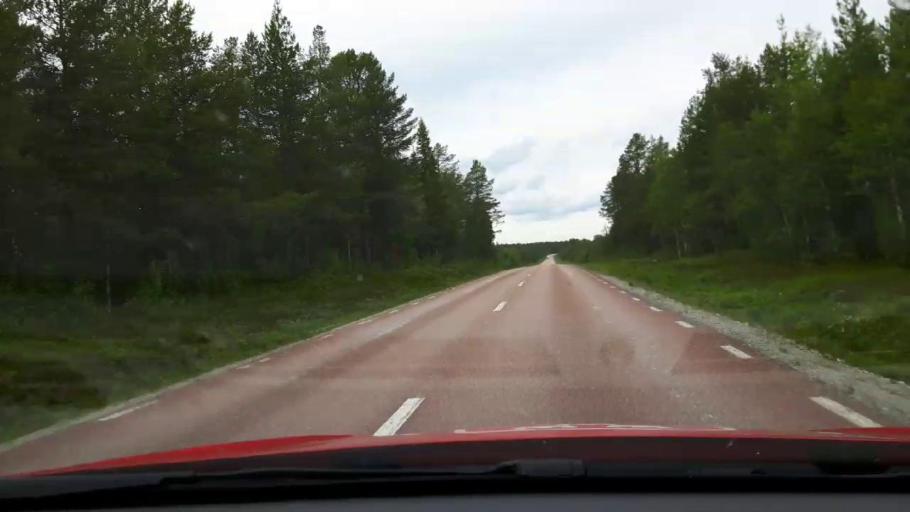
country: NO
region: Hedmark
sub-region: Engerdal
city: Engerdal
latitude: 62.4869
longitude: 12.6507
